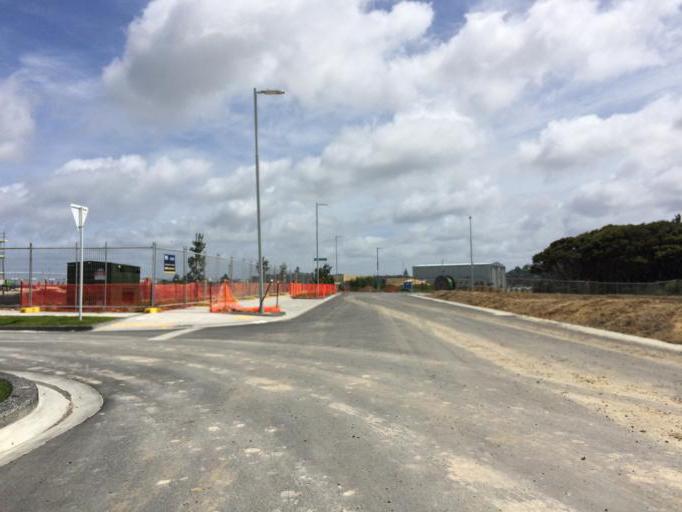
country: NZ
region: Auckland
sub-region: Auckland
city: Rosebank
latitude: -36.7939
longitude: 174.6691
